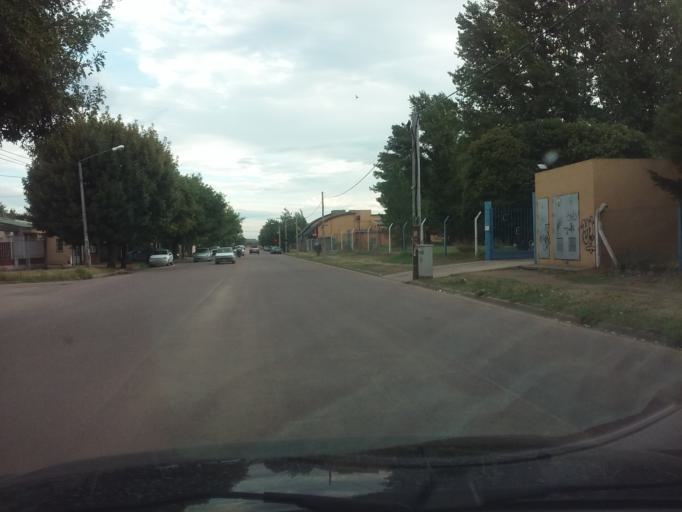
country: AR
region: La Pampa
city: Santa Rosa
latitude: -36.6429
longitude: -64.2933
